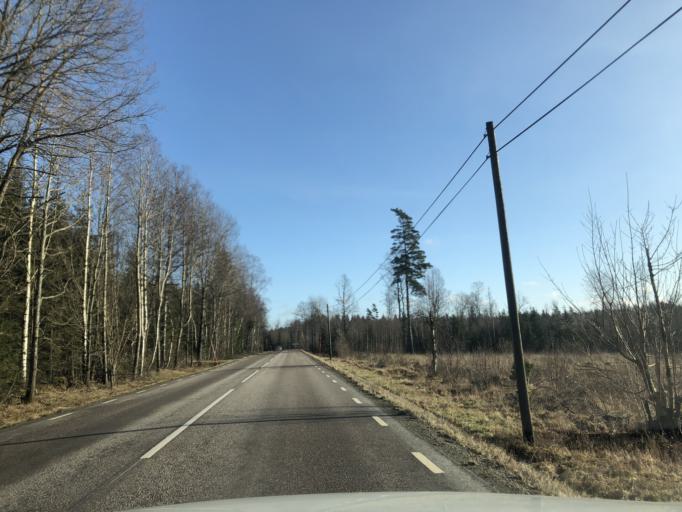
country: SE
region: Vaestra Goetaland
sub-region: Ulricehamns Kommun
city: Ulricehamn
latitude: 57.6654
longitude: 13.4086
